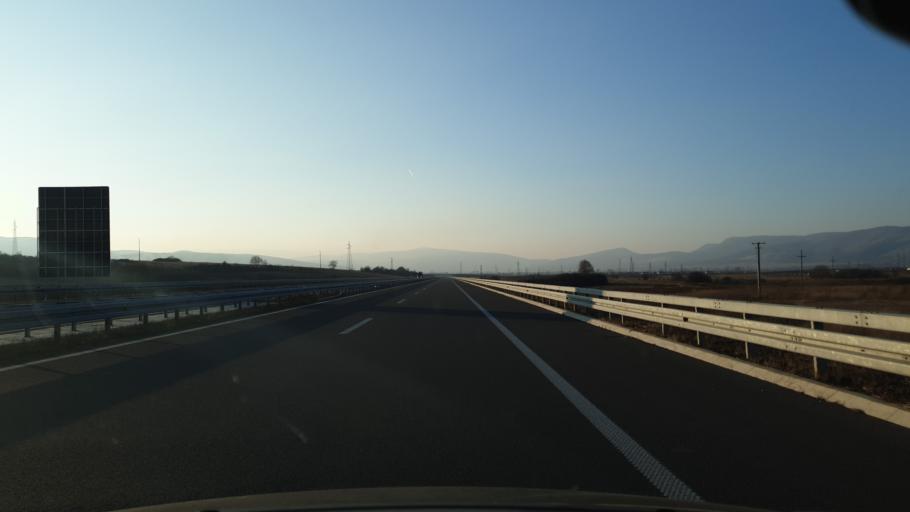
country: RS
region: Central Serbia
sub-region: Pirotski Okrug
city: Pirot
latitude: 43.1230
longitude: 22.6072
